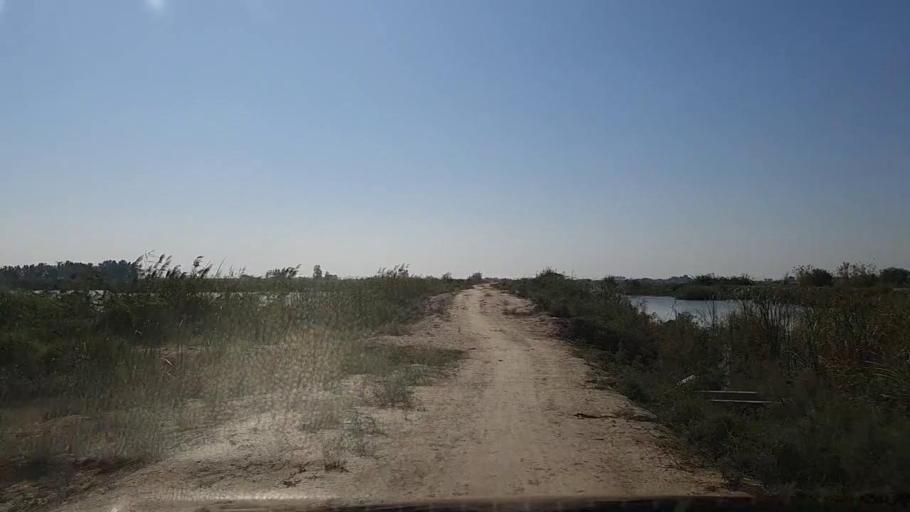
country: PK
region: Sindh
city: Thatta
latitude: 24.6735
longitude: 67.8887
